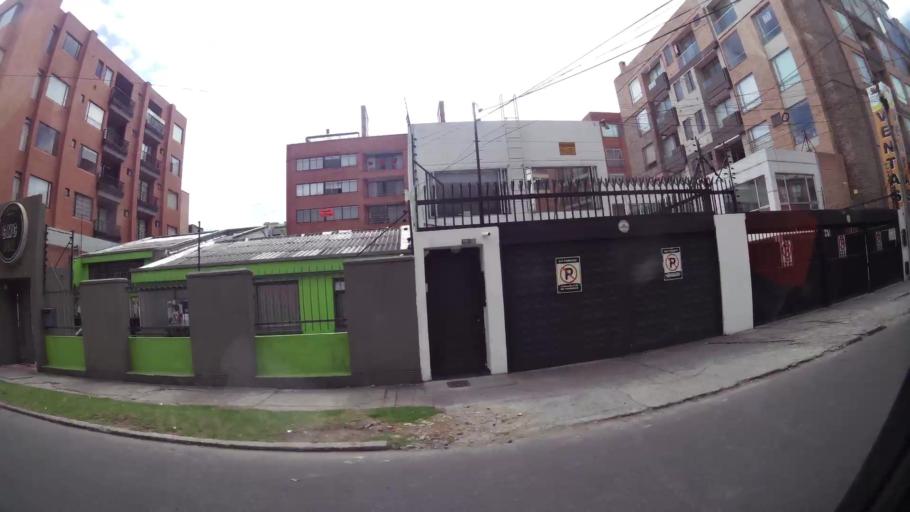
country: CO
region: Bogota D.C.
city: Barrio San Luis
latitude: 4.6989
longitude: -74.0474
